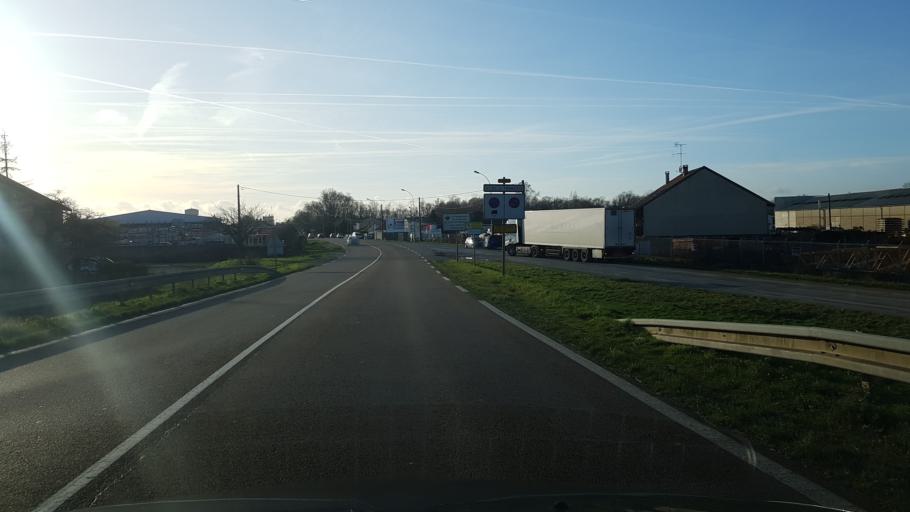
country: FR
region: Champagne-Ardenne
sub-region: Departement de la Marne
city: Vitry-le-Francois
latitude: 48.7350
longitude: 4.6093
